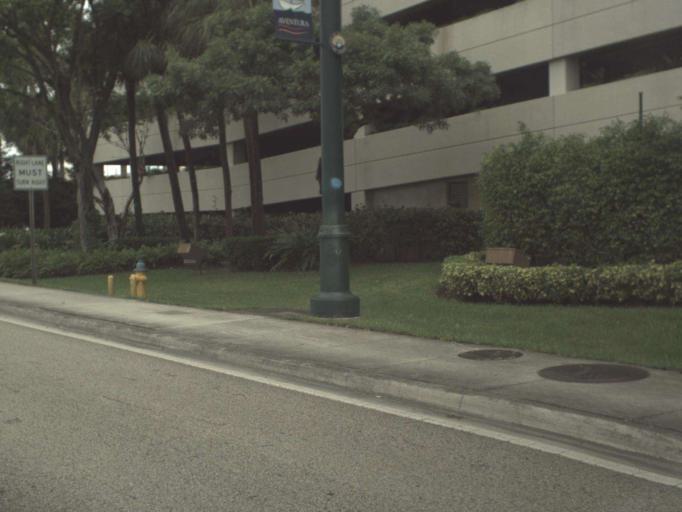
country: US
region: Florida
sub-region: Miami-Dade County
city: Aventura
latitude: 25.9563
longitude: -80.1467
